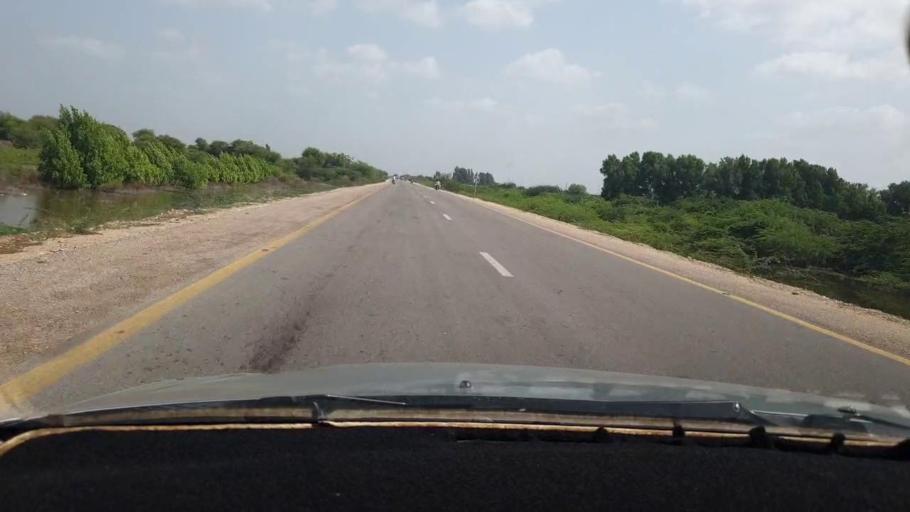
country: PK
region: Sindh
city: Digri
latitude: 25.1129
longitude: 69.1590
